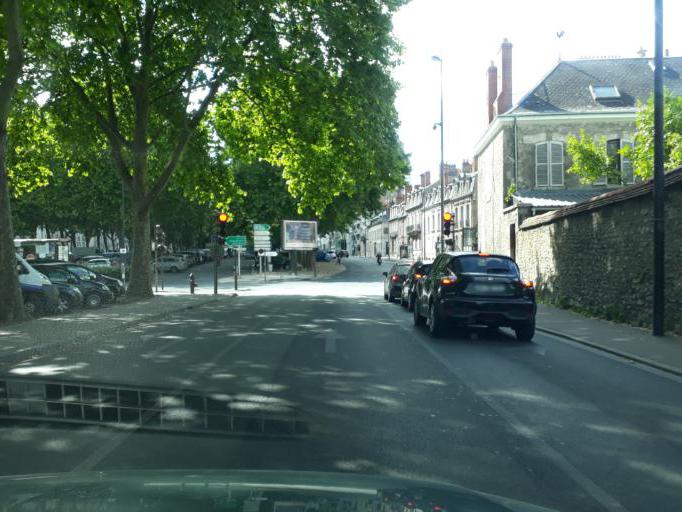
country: FR
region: Centre
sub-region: Departement du Loiret
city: Orleans
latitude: 47.9047
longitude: 1.9141
